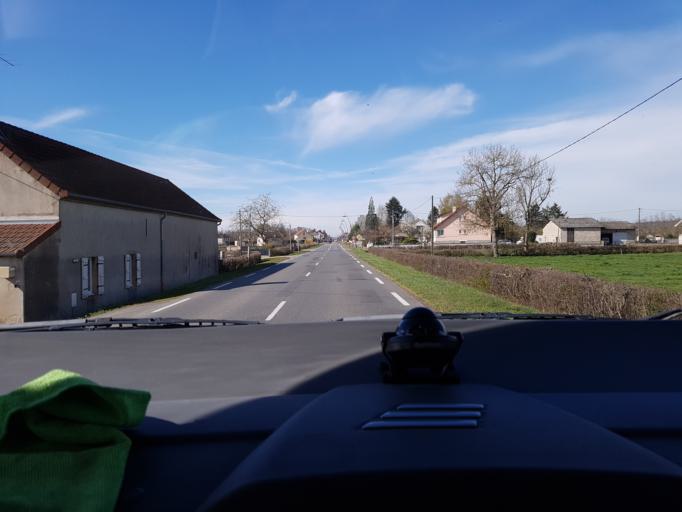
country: FR
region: Bourgogne
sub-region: Departement de Saone-et-Loire
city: Digoin
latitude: 46.5023
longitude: 4.0166
